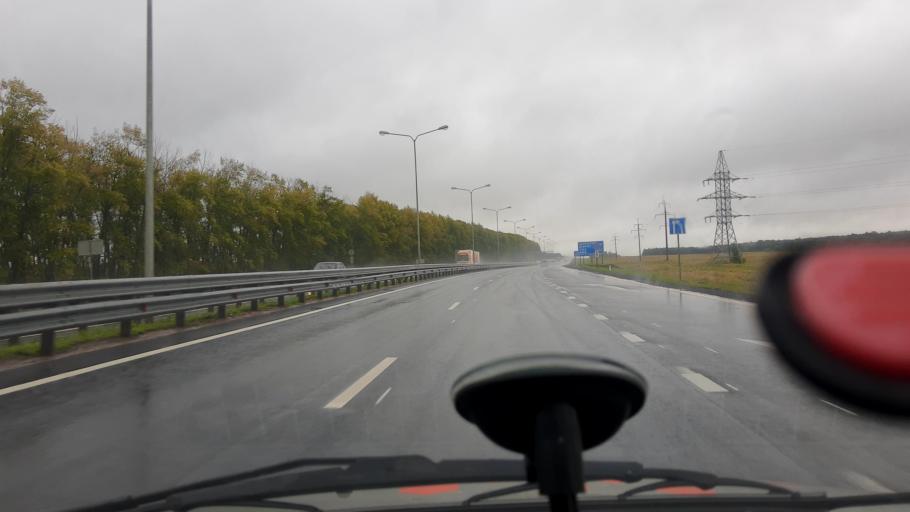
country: RU
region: Bashkortostan
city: Kushnarenkovo
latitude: 55.0568
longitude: 55.4323
